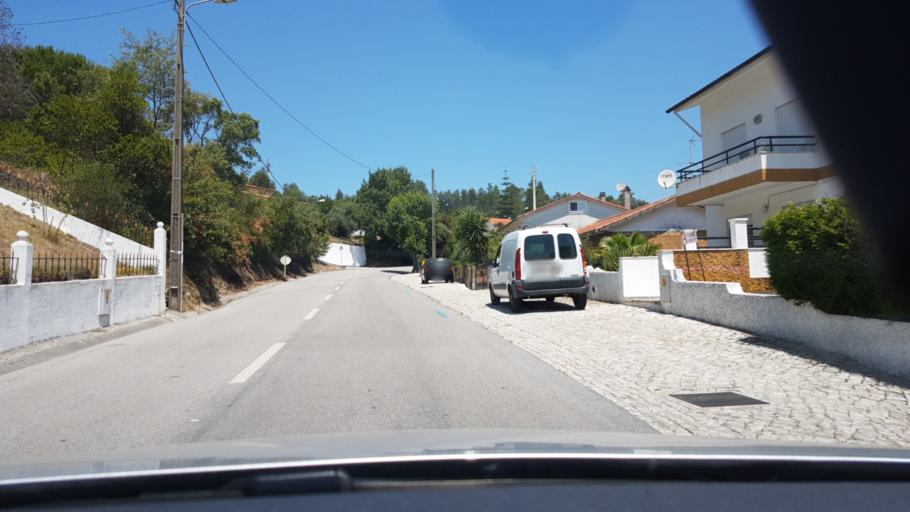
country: PT
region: Coimbra
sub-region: Coimbra
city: Coimbra
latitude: 40.1760
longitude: -8.4538
